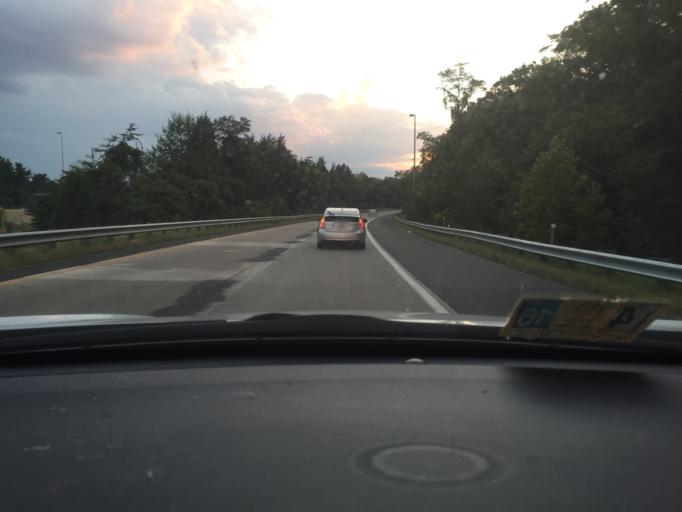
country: US
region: Virginia
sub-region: City of Fairfax
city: Fairfax
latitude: 38.8636
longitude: -77.3397
